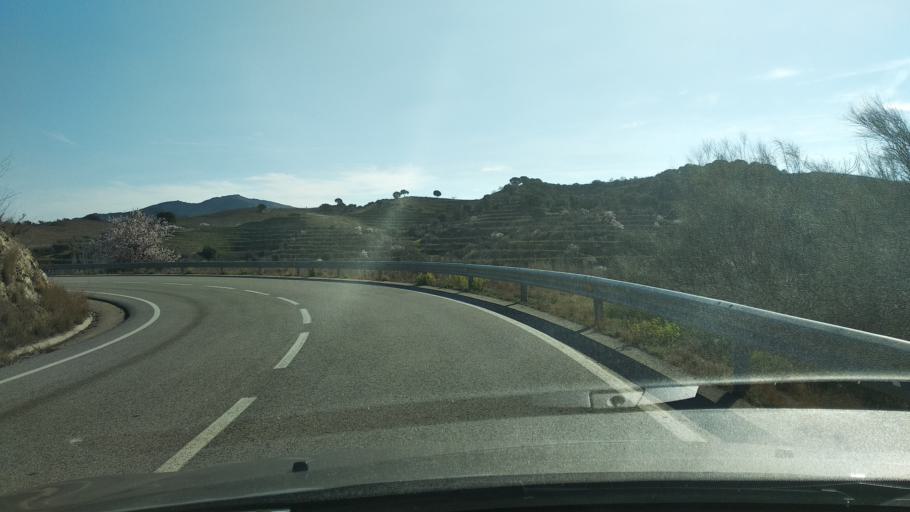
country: ES
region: Catalonia
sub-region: Provincia de Tarragona
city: Falset
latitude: 41.1895
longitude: 0.7725
